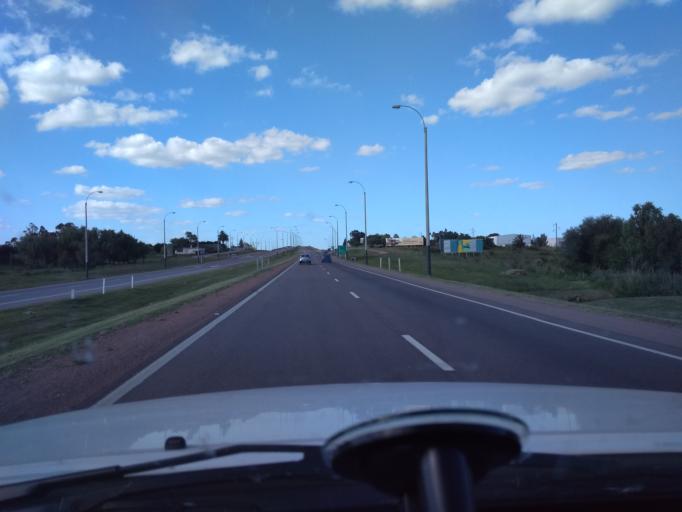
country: UY
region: Canelones
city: Las Piedras
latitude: -34.7278
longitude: -56.2479
